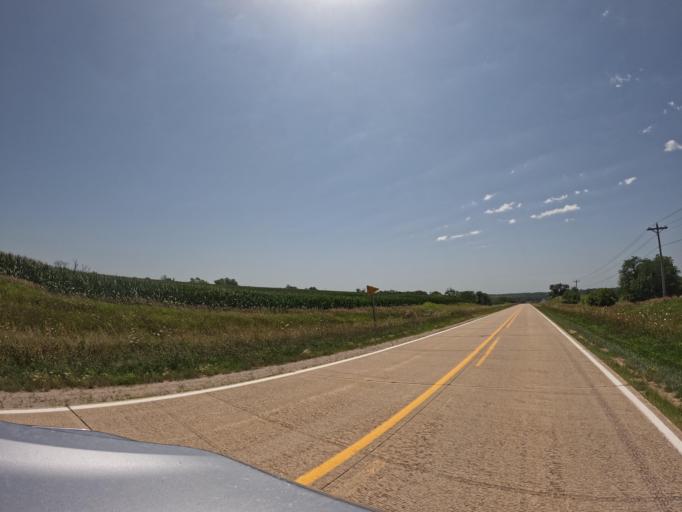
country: US
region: Iowa
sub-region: Henry County
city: Mount Pleasant
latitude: 40.9115
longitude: -91.5543
